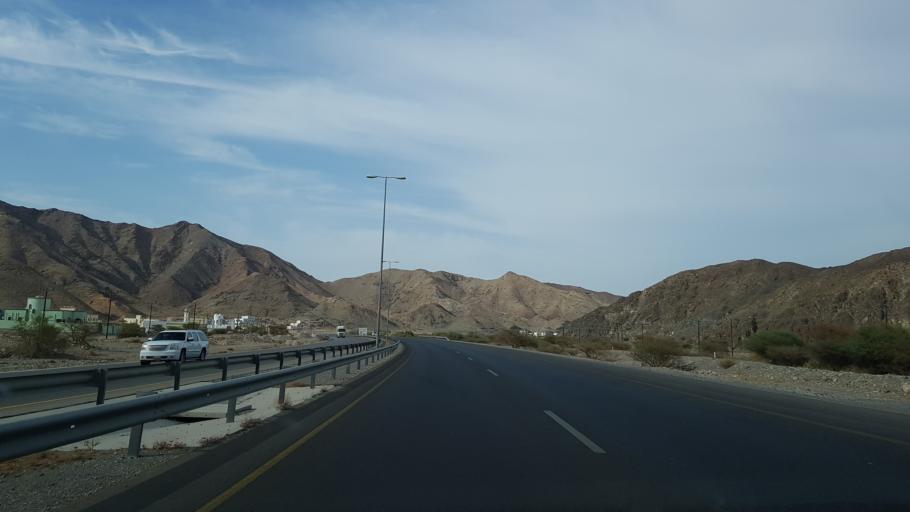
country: OM
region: Muhafazat ad Dakhiliyah
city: Bidbid
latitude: 23.4044
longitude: 58.0796
